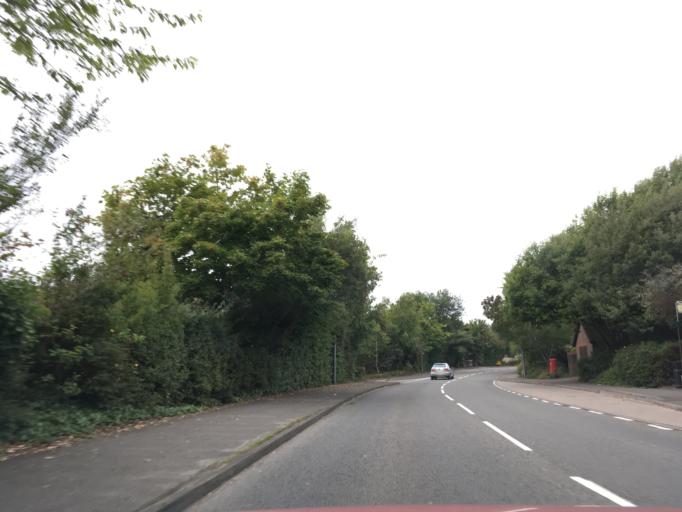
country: GB
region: Wales
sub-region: Caerphilly County Borough
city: Machen
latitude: 51.5345
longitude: -3.1434
